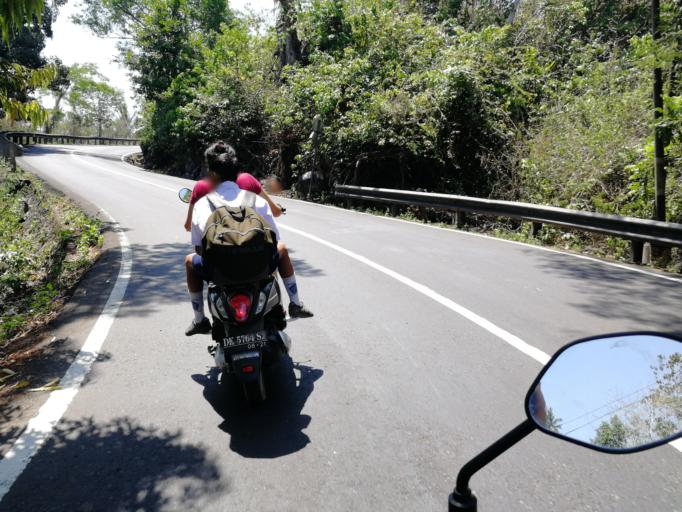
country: ID
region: Bali
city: Abang
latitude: -8.3915
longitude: 115.5971
